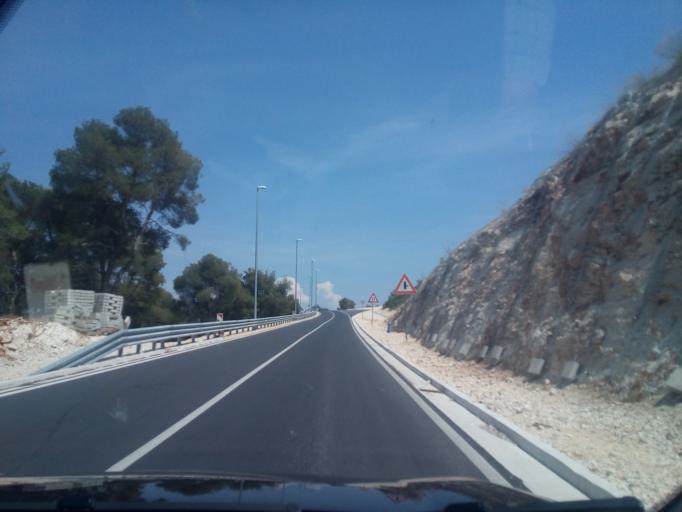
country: HR
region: Splitsko-Dalmatinska
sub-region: Grad Trogir
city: Trogir
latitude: 43.5163
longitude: 16.2666
